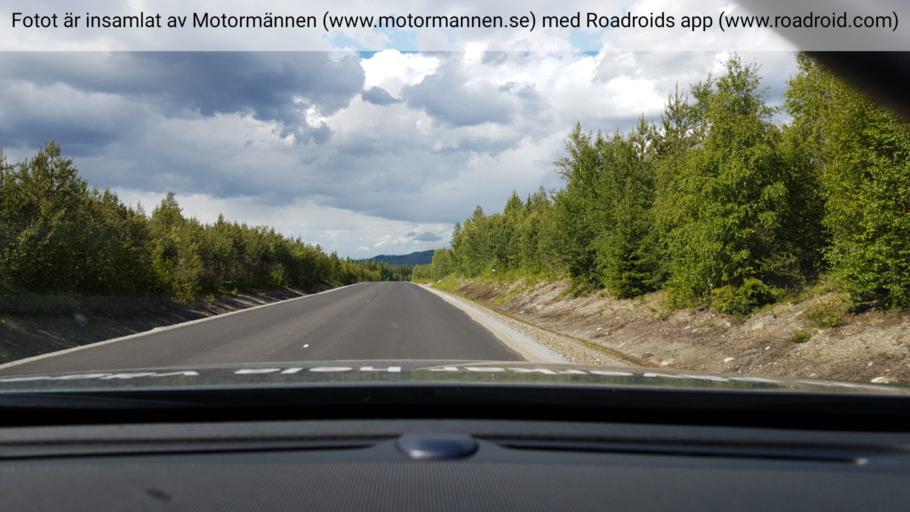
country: SE
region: Vaesterbotten
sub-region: Lycksele Kommun
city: Lycksele
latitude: 63.9957
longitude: 18.4749
